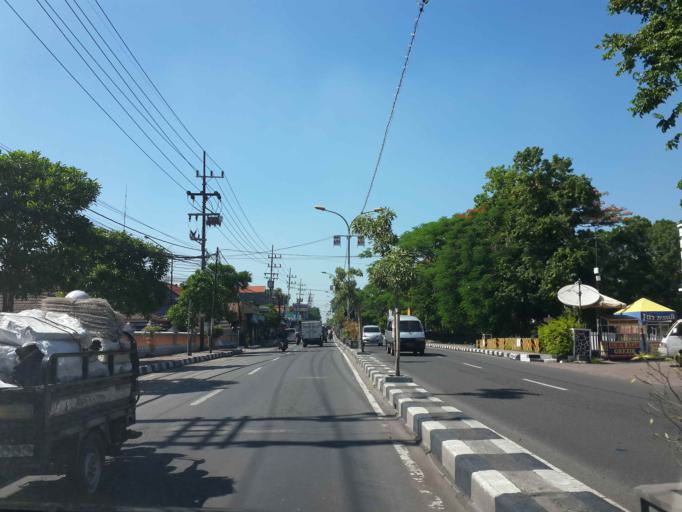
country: ID
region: East Java
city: Kebomas
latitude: -7.1778
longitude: 112.6509
